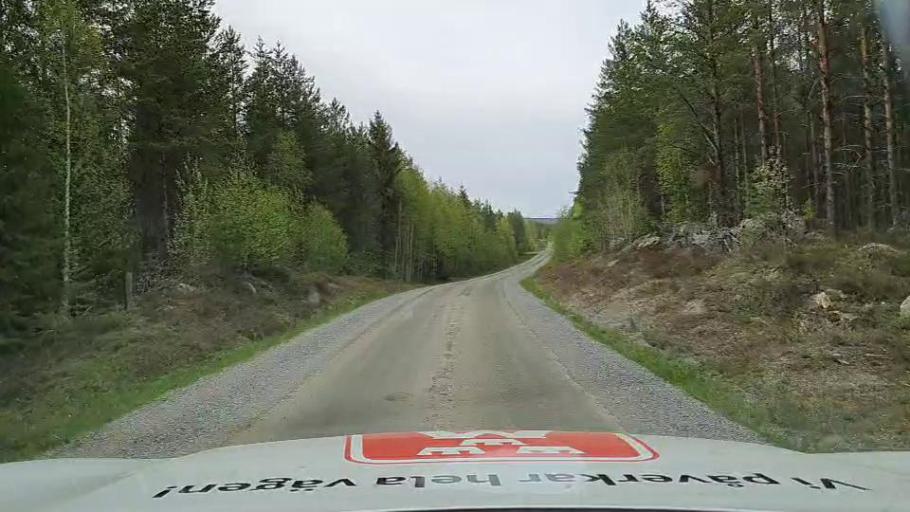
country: SE
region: Jaemtland
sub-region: Braecke Kommun
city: Braecke
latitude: 62.4704
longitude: 14.9159
